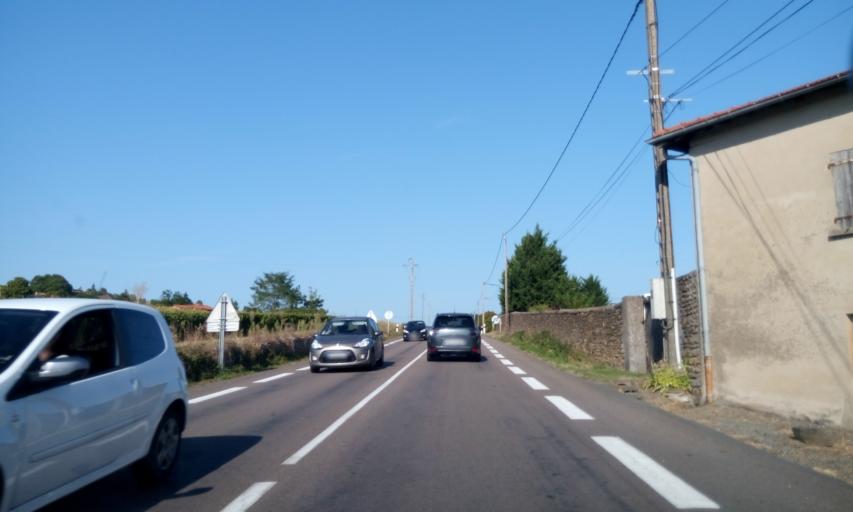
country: FR
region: Rhone-Alpes
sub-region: Departement du Rhone
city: Theize
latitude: 45.9121
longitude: 4.6069
